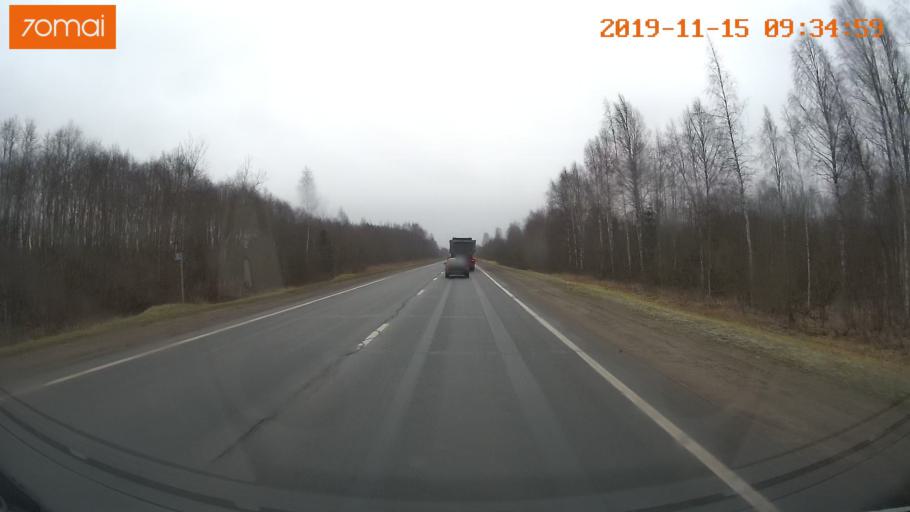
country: RU
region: Vologda
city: Sheksna
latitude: 59.2568
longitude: 38.3905
